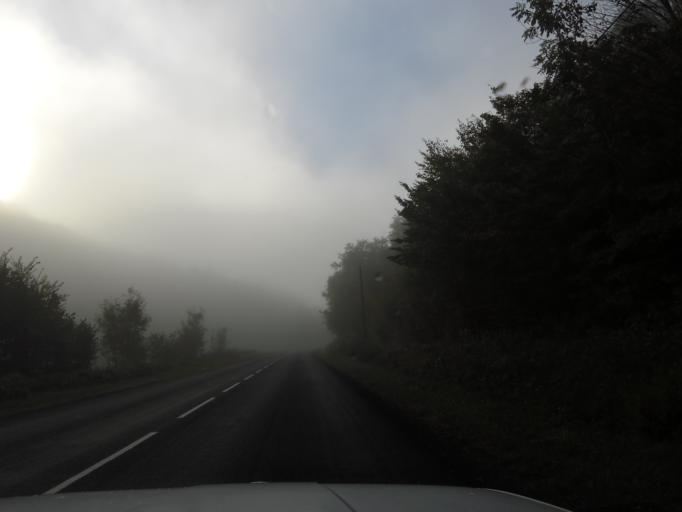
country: FR
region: Rhone-Alpes
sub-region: Departement de l'Isere
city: Creys-Mepieu
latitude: 45.7568
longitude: 5.4976
